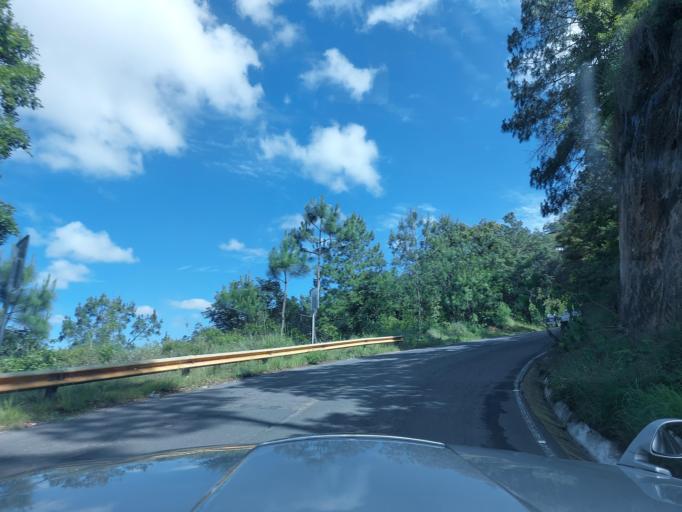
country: GT
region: Chimaltenango
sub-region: Municipio de Santa Cruz Balanya
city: Santa Cruz Balanya
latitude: 14.6966
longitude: -90.9002
